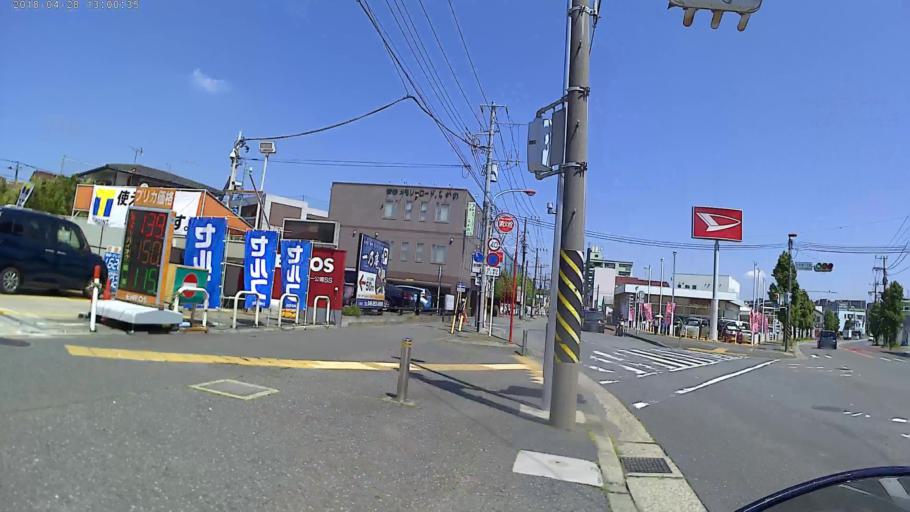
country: JP
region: Kanagawa
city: Yokosuka
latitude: 35.2531
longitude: 139.6755
